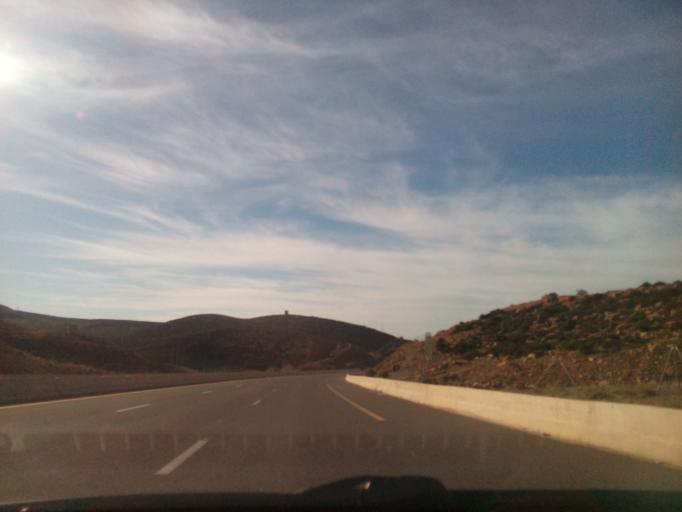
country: DZ
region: Tlemcen
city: Beni Mester
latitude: 34.9122
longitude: -1.3978
